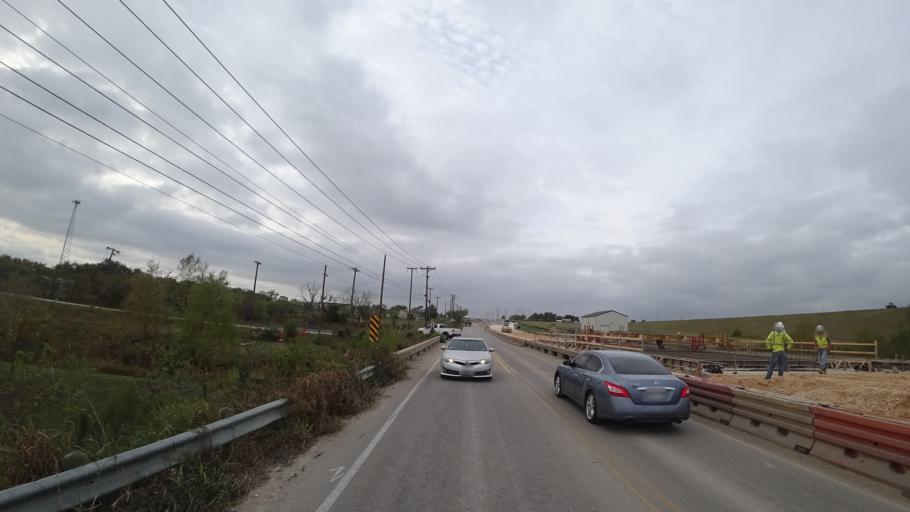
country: US
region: Texas
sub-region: Travis County
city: Pflugerville
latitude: 30.4384
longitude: -97.5671
